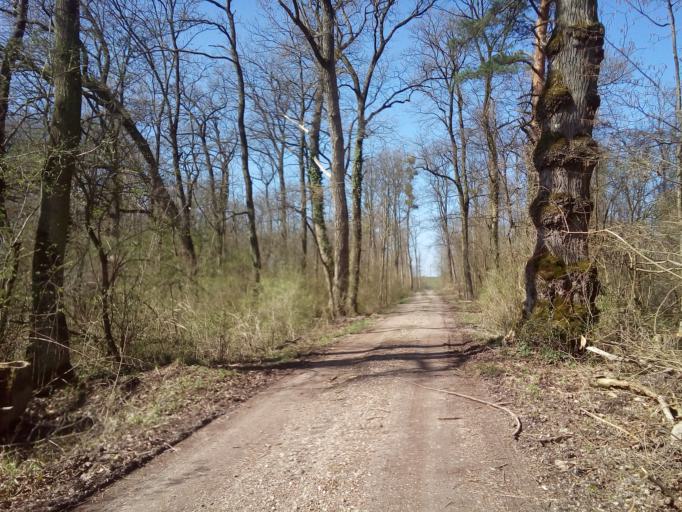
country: DE
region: Baden-Wuerttemberg
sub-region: Freiburg Region
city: Rheinau
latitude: 48.6713
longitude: 7.9140
